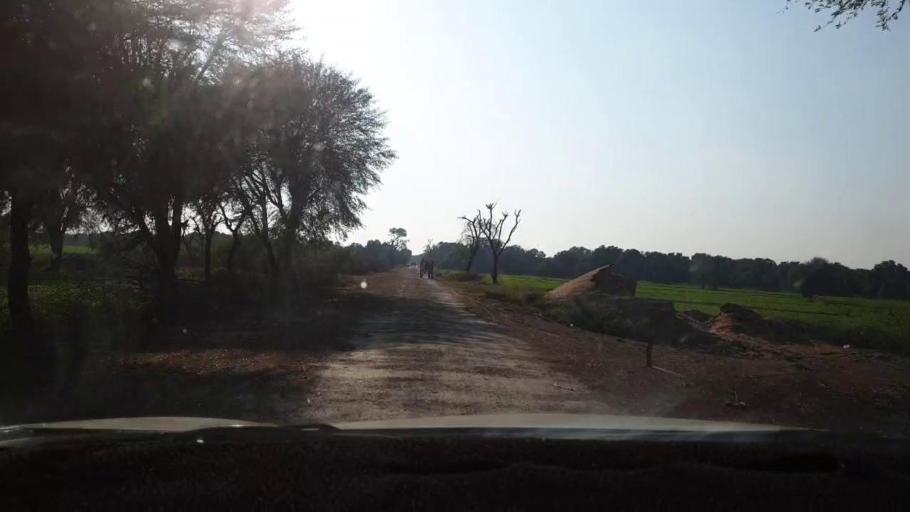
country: PK
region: Sindh
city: Berani
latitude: 25.7641
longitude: 68.7648
